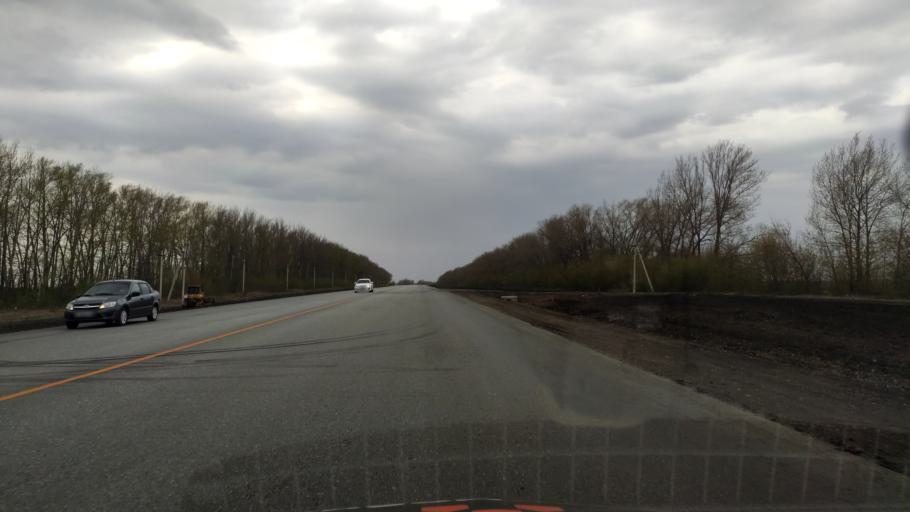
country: RU
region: Kursk
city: Gorshechnoye
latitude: 51.5480
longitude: 38.0914
